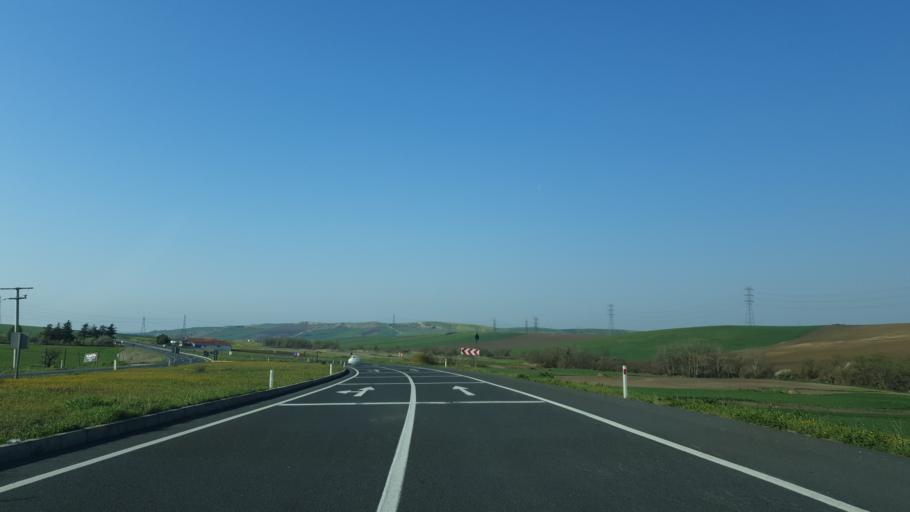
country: TR
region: Tekirdag
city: Corlu
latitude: 41.0867
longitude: 27.7435
